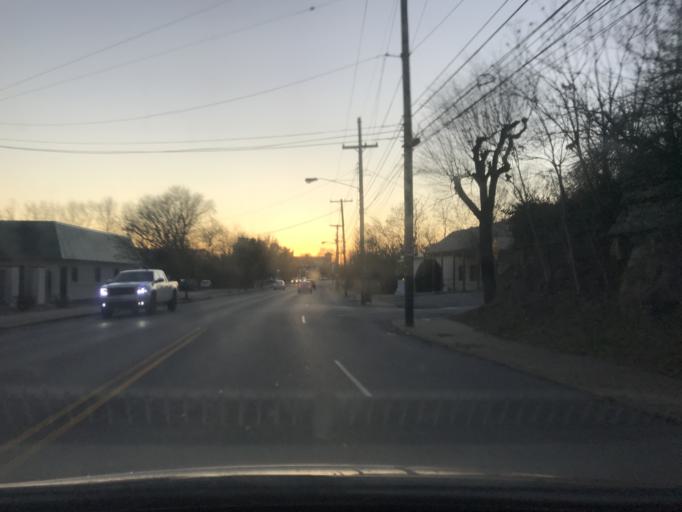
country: US
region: Kentucky
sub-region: Jefferson County
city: Audubon Park
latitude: 38.2351
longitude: -85.7291
